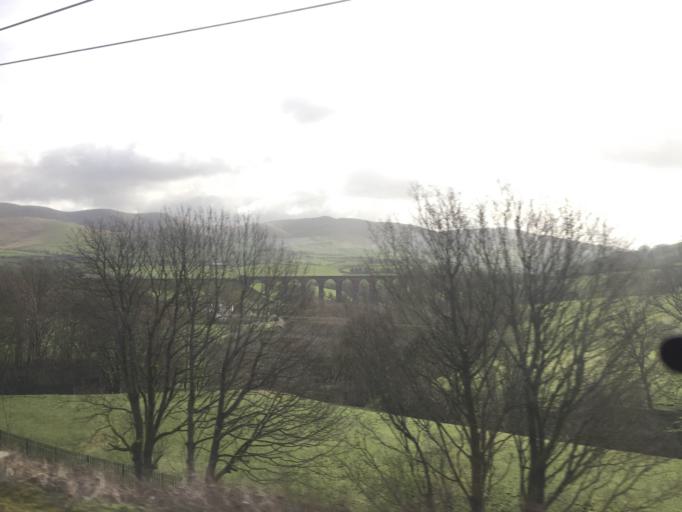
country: GB
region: England
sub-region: Cumbria
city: Sedbergh
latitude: 54.3637
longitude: -2.5991
